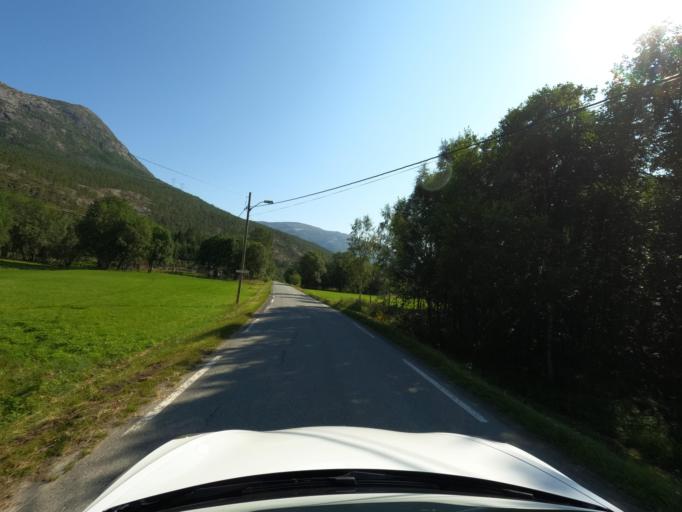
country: NO
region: Nordland
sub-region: Narvik
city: Narvik
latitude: 68.1882
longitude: 17.5520
